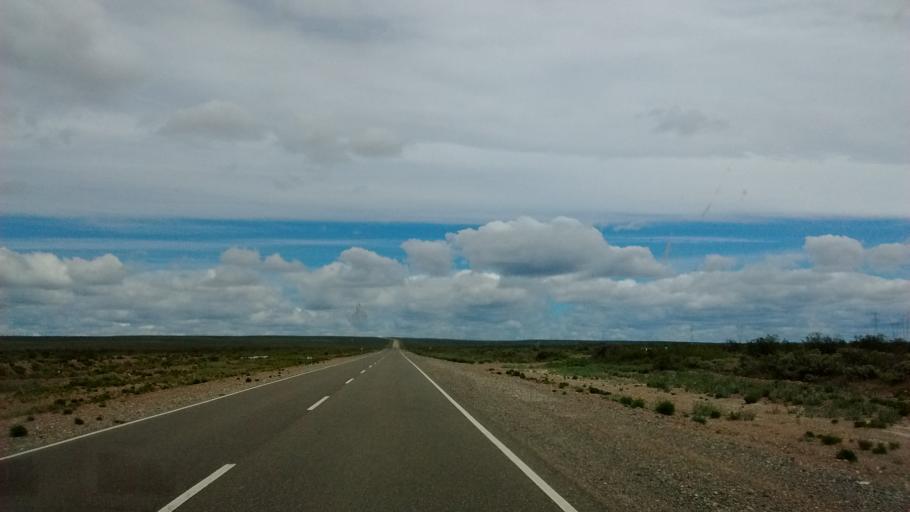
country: AR
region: Neuquen
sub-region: Departamento de Picun Leufu
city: Picun Leufu
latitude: -39.7166
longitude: -69.5300
